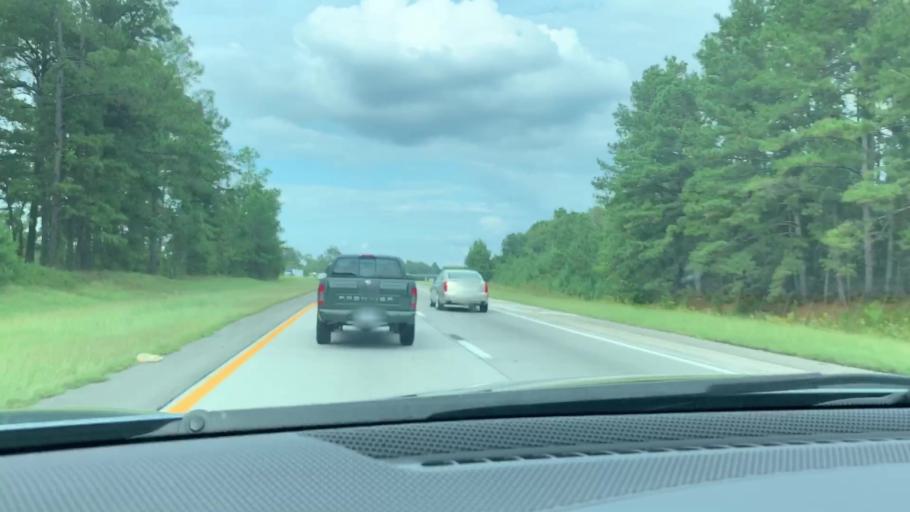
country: US
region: South Carolina
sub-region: Dorchester County
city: Saint George
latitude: 33.1249
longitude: -80.6400
